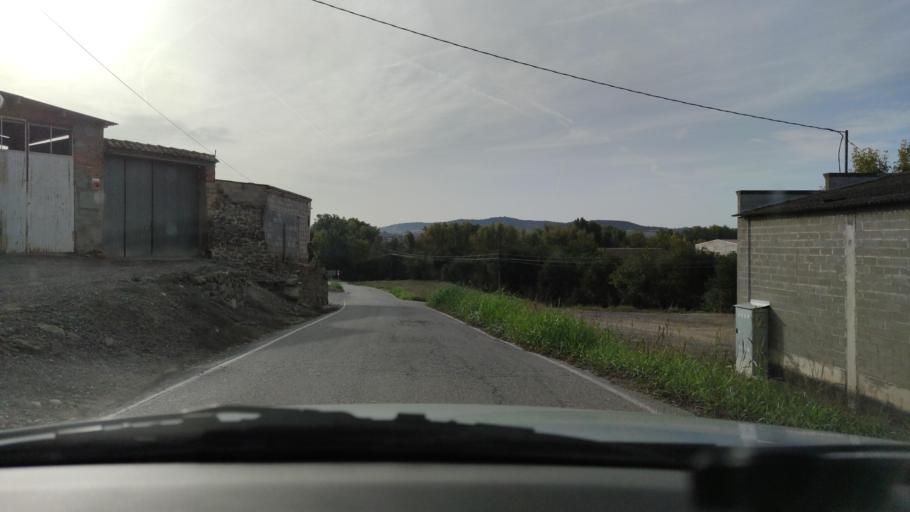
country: ES
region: Catalonia
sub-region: Provincia de Lleida
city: Artesa de Segre
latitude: 41.9047
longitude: 1.0399
